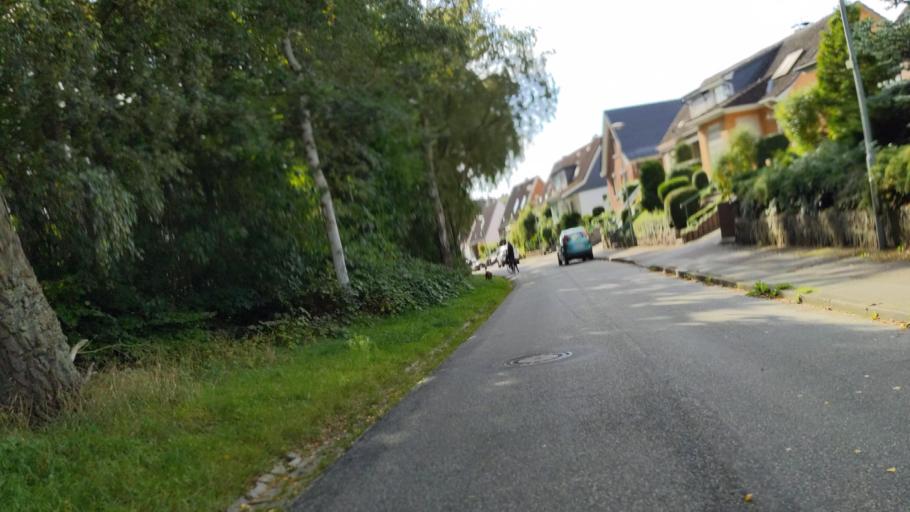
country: DE
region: Mecklenburg-Vorpommern
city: Selmsdorf
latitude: 53.9075
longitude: 10.7949
